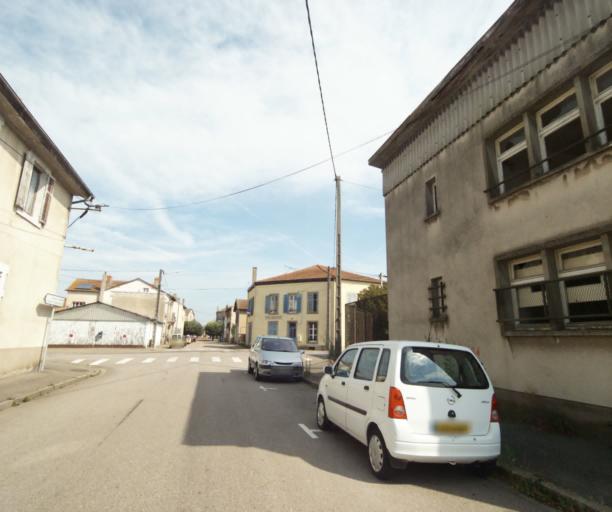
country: FR
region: Lorraine
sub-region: Departement de Meurthe-et-Moselle
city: Luneville
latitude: 48.5891
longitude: 6.5088
